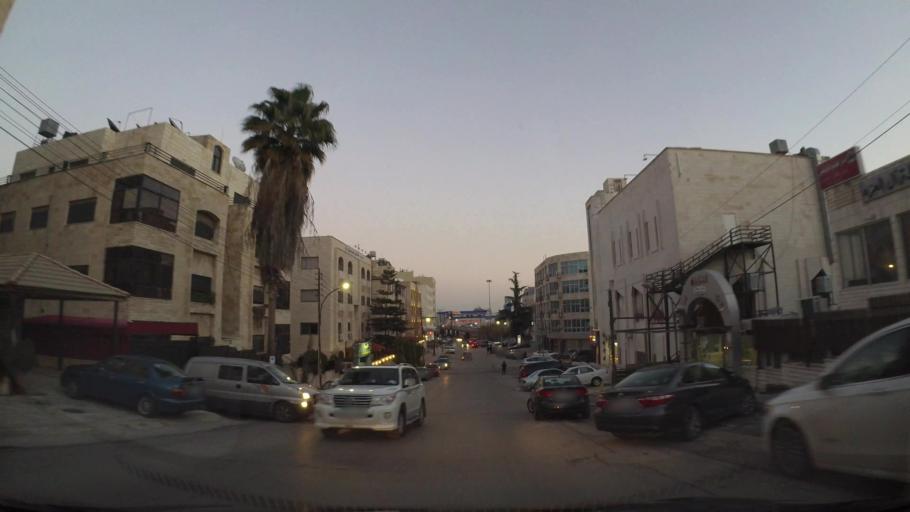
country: JO
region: Amman
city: Al Jubayhah
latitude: 31.9842
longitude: 35.8921
